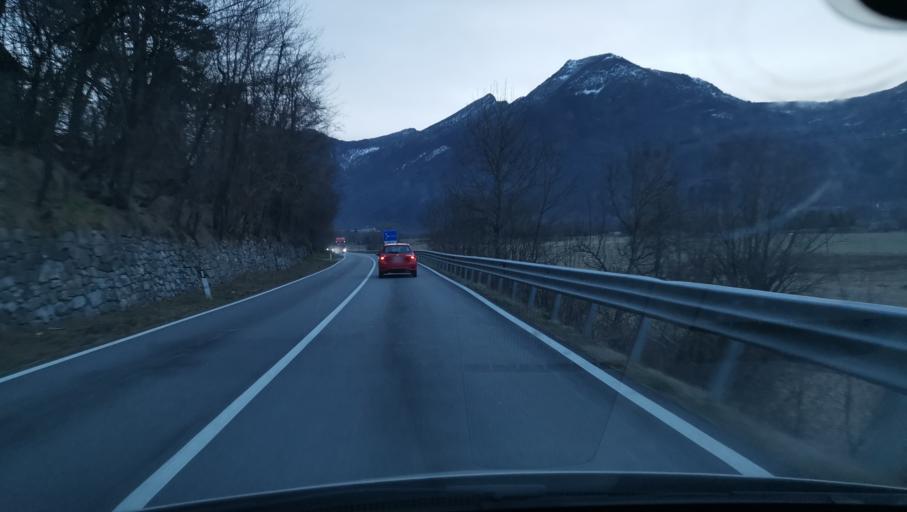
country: IT
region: Piedmont
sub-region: Provincia di Cuneo
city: Demonte
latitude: 44.3138
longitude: 7.3390
